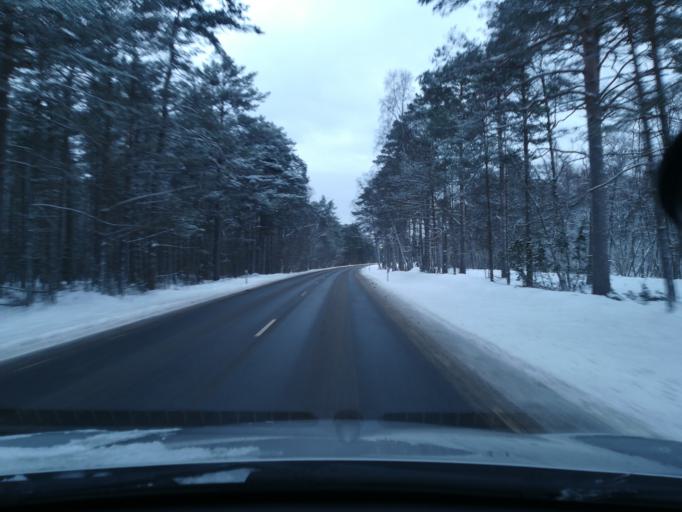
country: EE
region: Harju
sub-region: Paldiski linn
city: Paldiski
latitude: 59.3924
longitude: 24.2418
